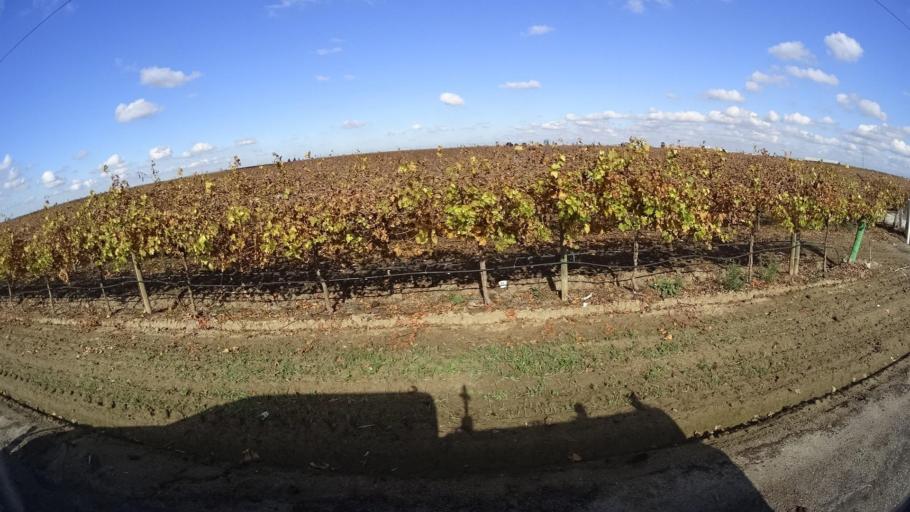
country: US
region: California
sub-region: Kern County
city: McFarland
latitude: 35.6816
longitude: -119.2523
